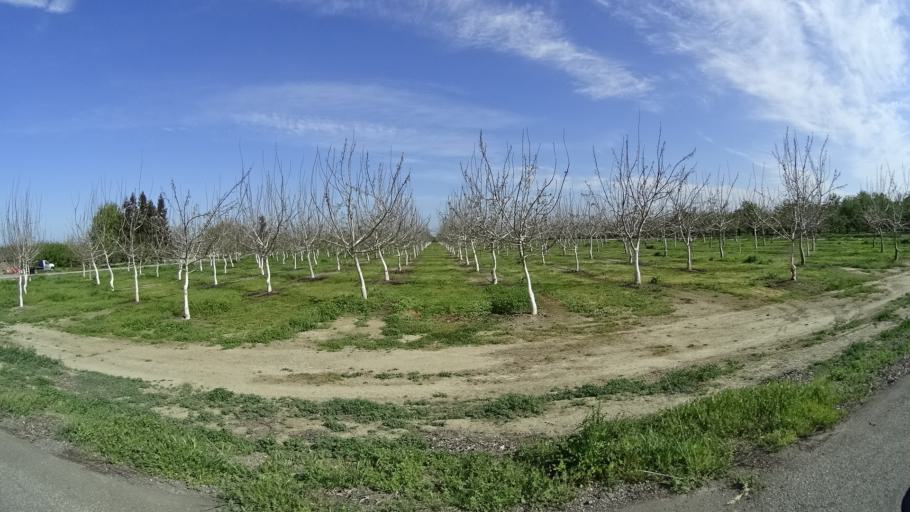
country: US
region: California
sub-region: Glenn County
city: Hamilton City
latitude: 39.6234
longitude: -122.0236
